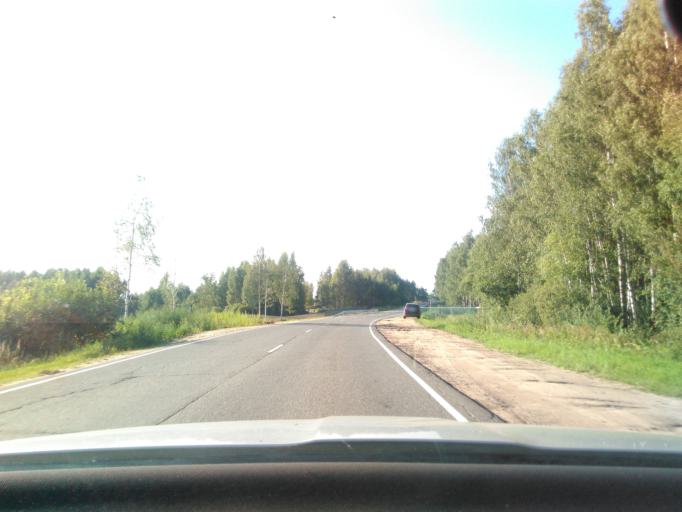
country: RU
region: Tverskaya
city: Zavidovo
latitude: 56.5949
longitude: 36.5396
